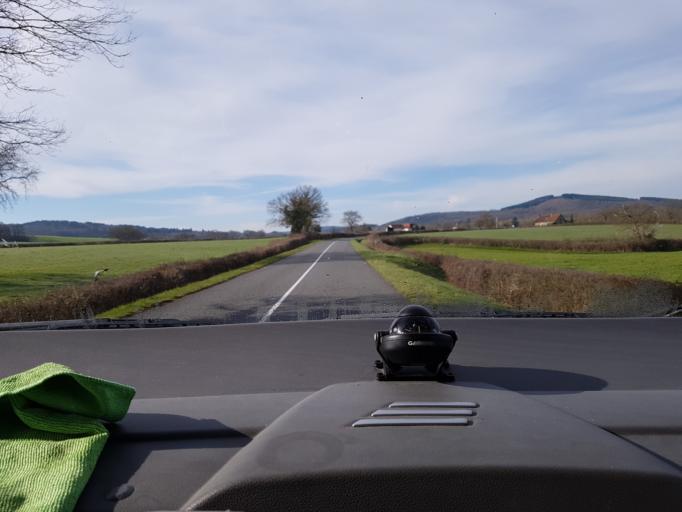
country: FR
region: Bourgogne
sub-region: Departement de Saone-et-Loire
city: Toulon-sur-Arroux
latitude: 46.7556
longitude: 4.1350
